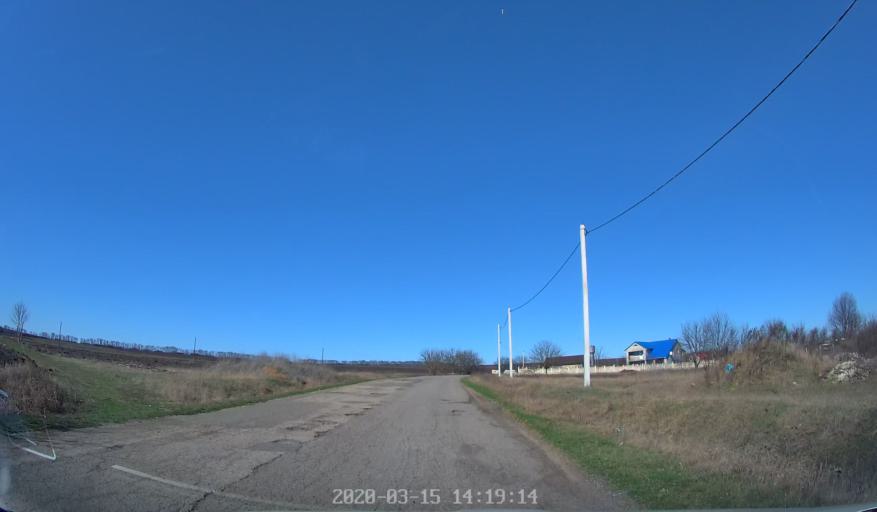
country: MD
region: Orhei
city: Orhei
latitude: 47.3030
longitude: 28.9157
